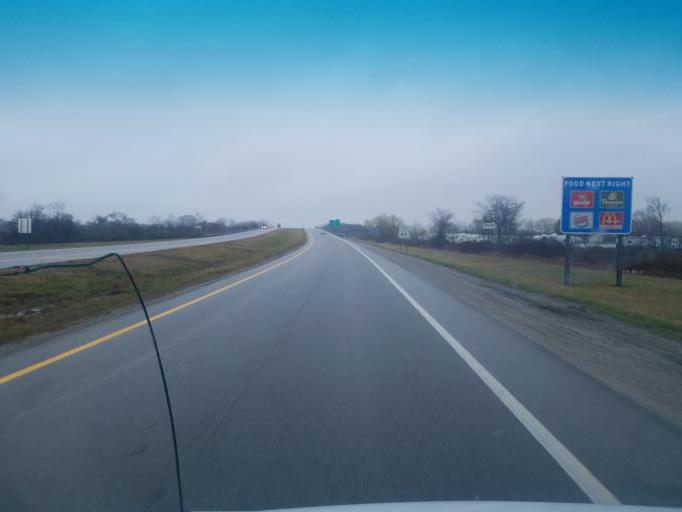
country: US
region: Ohio
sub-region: Wood County
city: Bowling Green
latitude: 41.3492
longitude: -83.6663
